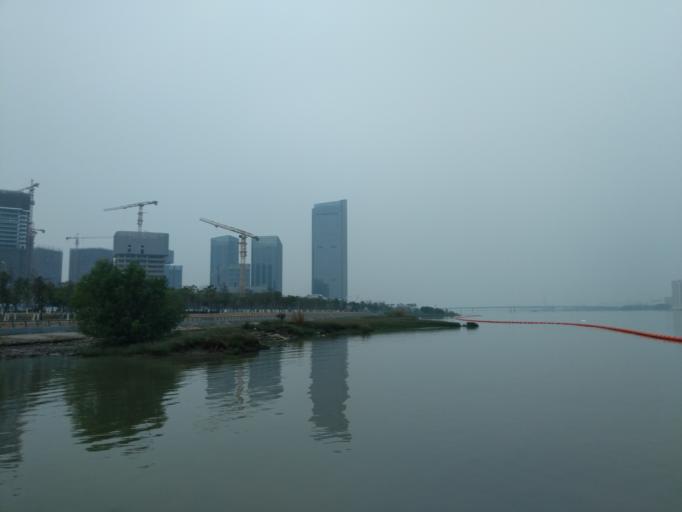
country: CN
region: Guangdong
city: Hengli
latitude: 22.7684
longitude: 113.5244
